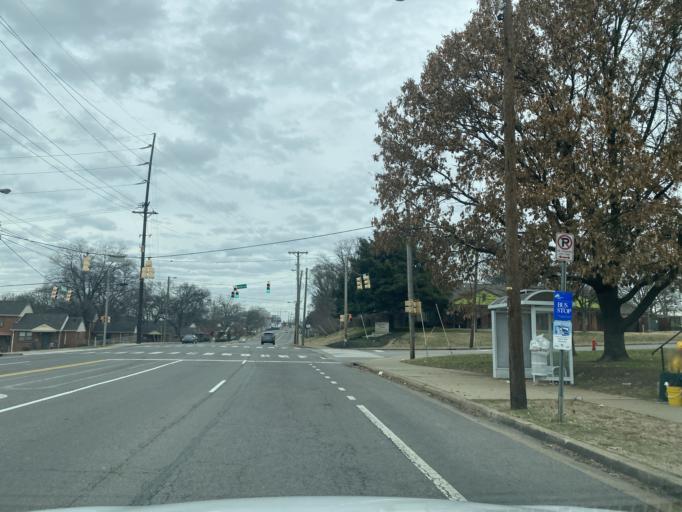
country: US
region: Tennessee
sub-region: Davidson County
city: Nashville
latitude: 36.1394
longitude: -86.7876
